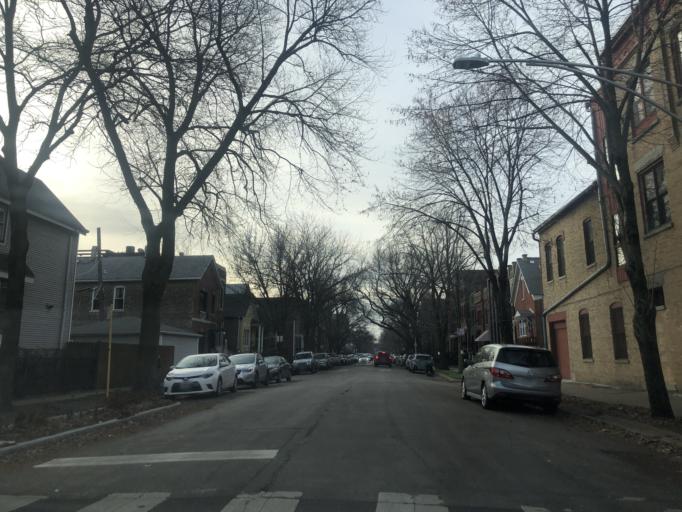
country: US
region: Illinois
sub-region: Cook County
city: Chicago
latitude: 41.9125
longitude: -87.6726
